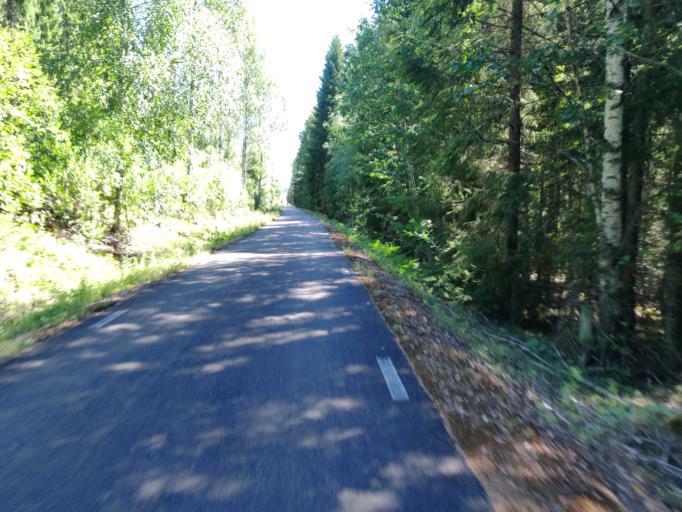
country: SE
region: Vaermland
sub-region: Munkfors Kommun
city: Munkfors
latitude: 59.9500
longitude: 13.5787
